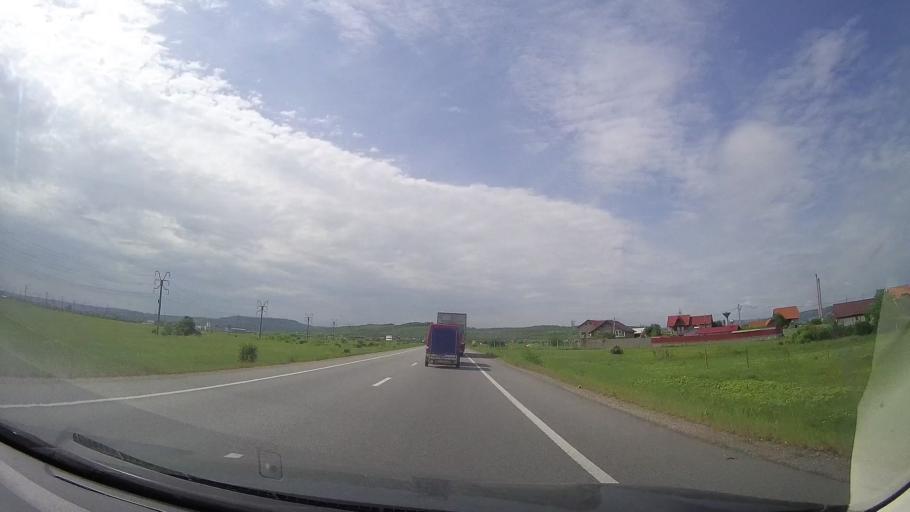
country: RO
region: Mehedinti
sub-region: Comuna Simian
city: Dudasu
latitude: 44.6501
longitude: 22.6910
